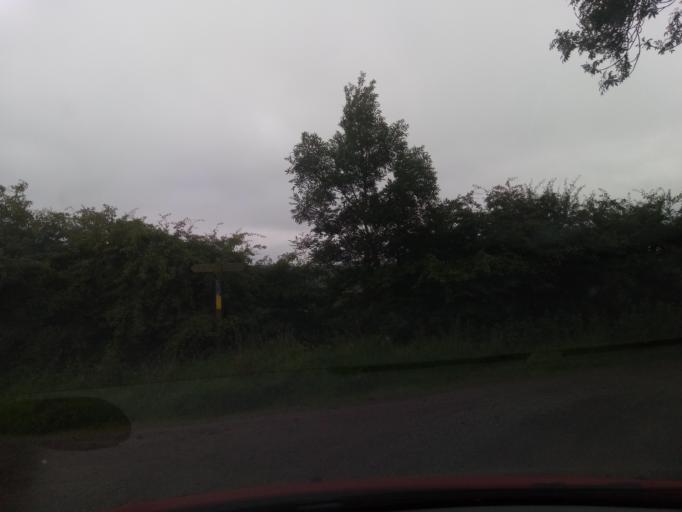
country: GB
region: England
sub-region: Northumberland
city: Otterburn
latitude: 55.2749
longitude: -2.0894
